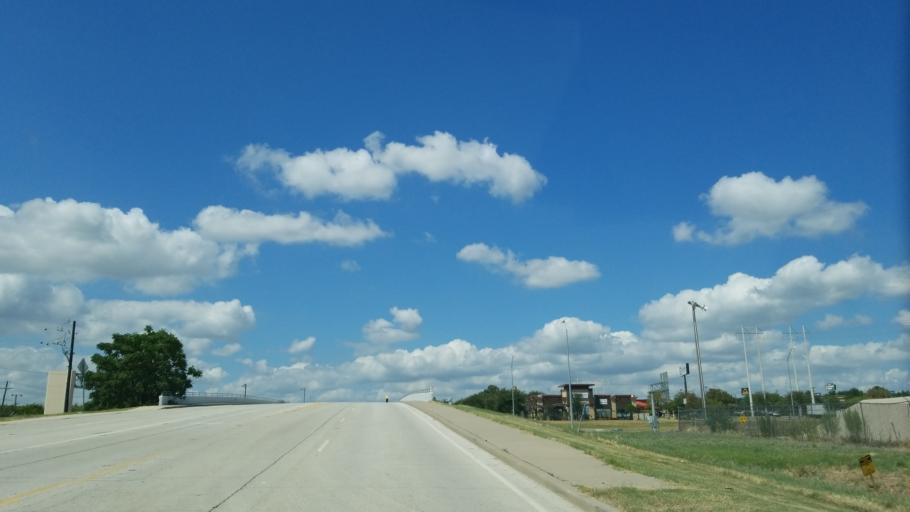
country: US
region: Texas
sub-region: Tarrant County
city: Grapevine
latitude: 32.9200
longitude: -97.0894
